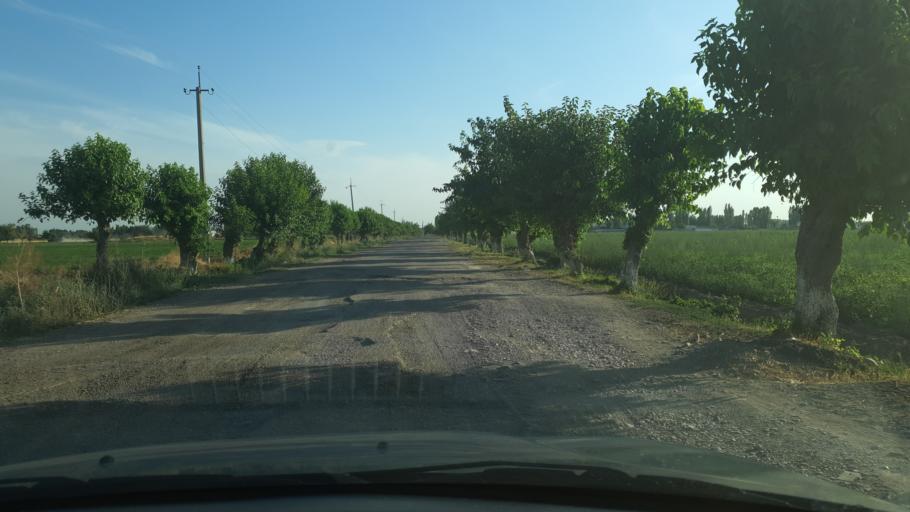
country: UZ
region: Toshkent
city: Tuytepa
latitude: 41.0932
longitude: 69.3706
